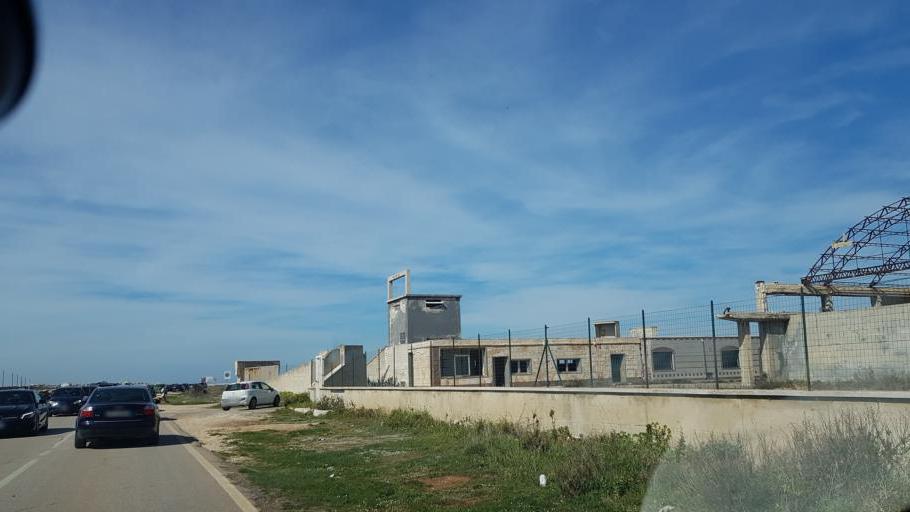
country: IT
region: Apulia
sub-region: Provincia di Brindisi
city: Pezze di Greco
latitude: 40.8603
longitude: 17.4302
